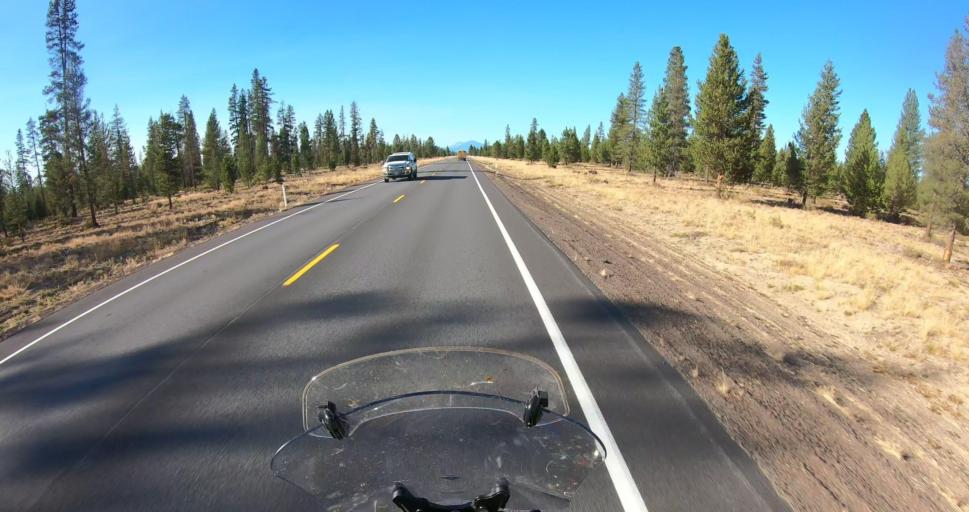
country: US
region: Oregon
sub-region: Deschutes County
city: La Pine
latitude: 43.5933
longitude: -121.4938
